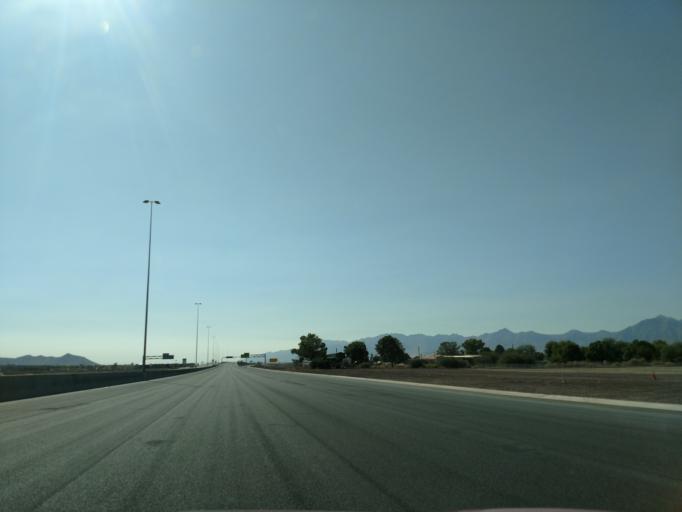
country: US
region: Arizona
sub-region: Maricopa County
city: Laveen
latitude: 33.3863
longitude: -112.1912
